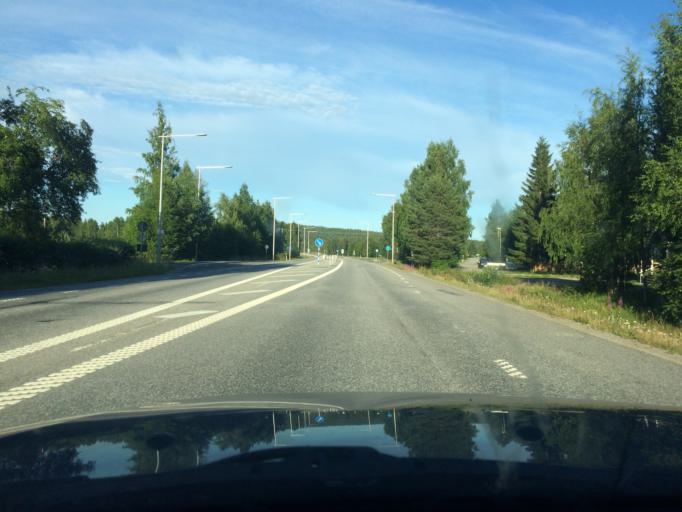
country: SE
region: Norrbotten
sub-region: Pitea Kommun
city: Bergsviken
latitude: 65.3146
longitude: 21.3280
